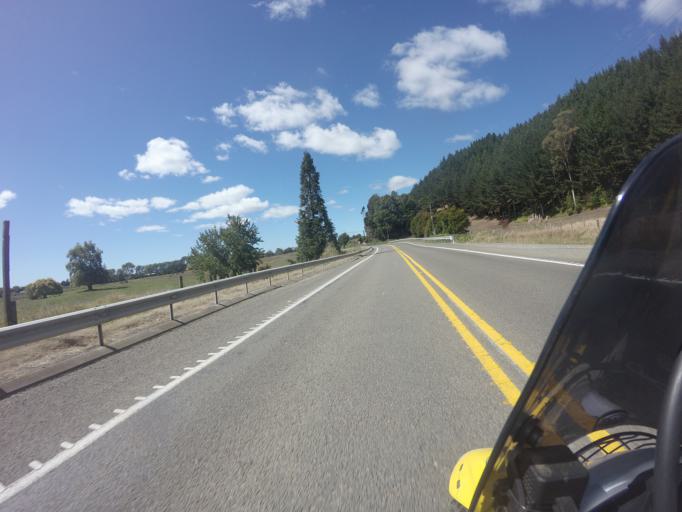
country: NZ
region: Bay of Plenty
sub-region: Whakatane District
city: Edgecumbe
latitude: -37.9993
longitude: 176.8704
